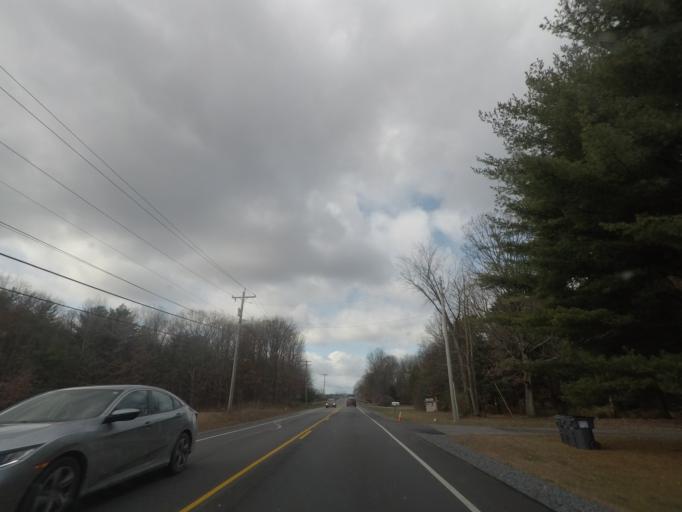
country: US
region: New York
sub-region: Saratoga County
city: Ballston Spa
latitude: 43.0126
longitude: -73.7959
